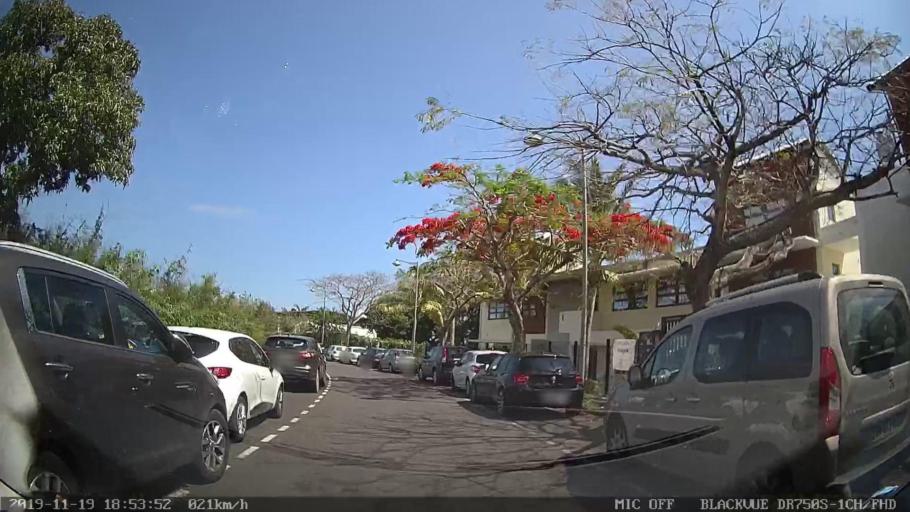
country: RE
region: Reunion
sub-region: Reunion
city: Sainte-Marie
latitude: -20.9041
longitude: 55.5029
